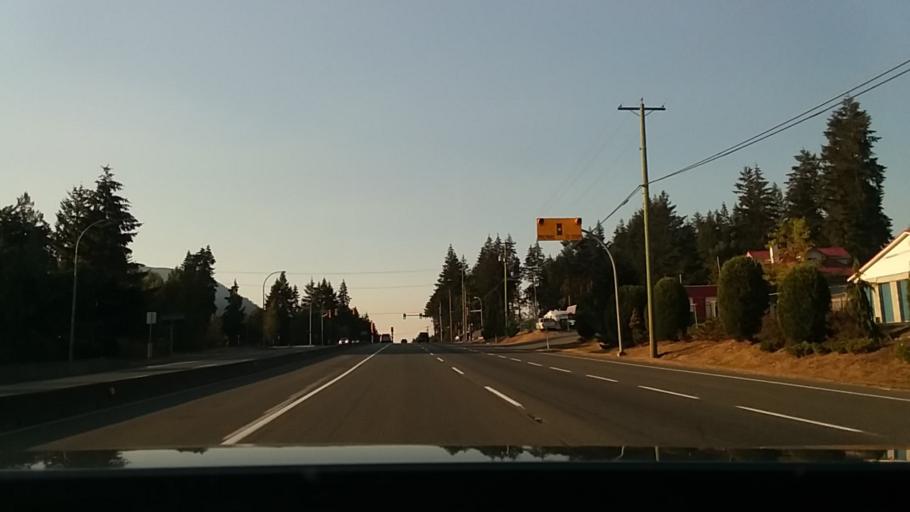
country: CA
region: British Columbia
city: Duncan
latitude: 48.8151
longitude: -123.7180
